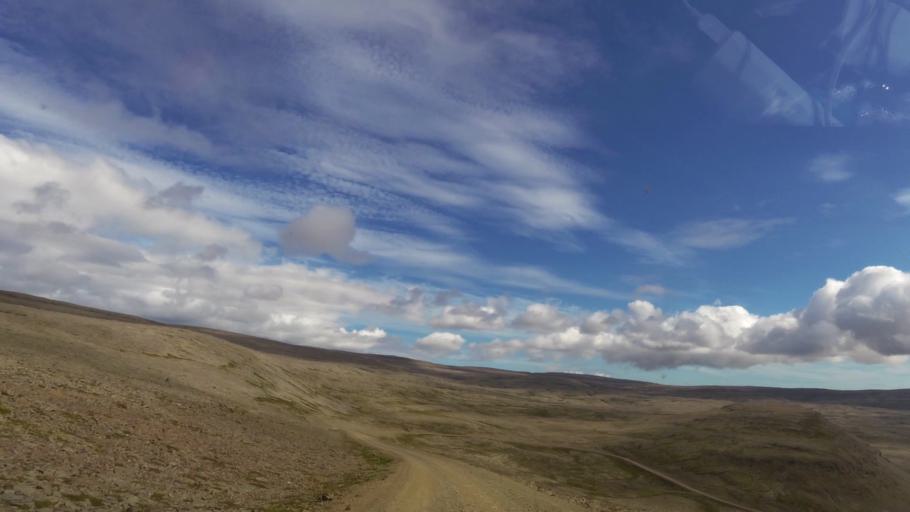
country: IS
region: West
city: Olafsvik
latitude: 65.6187
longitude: -24.3147
